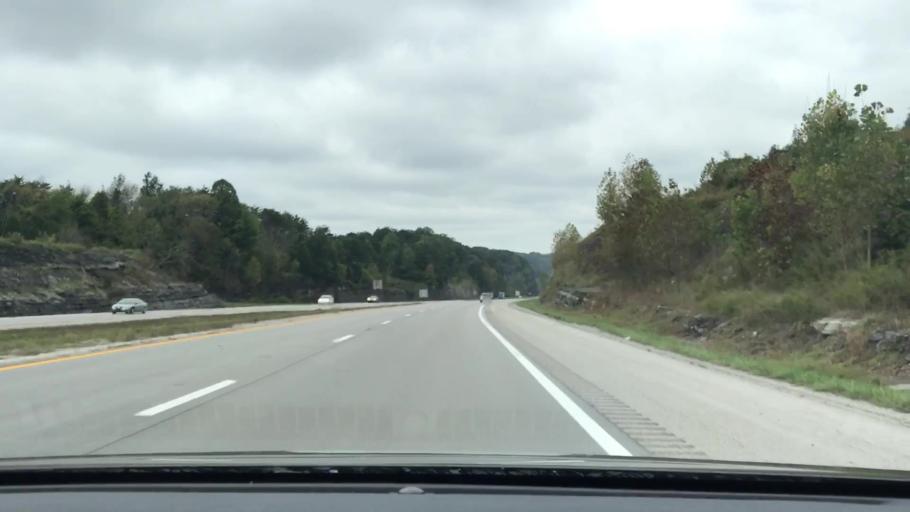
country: US
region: Kentucky
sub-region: Pulaski County
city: Somerset
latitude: 37.1002
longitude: -84.6721
